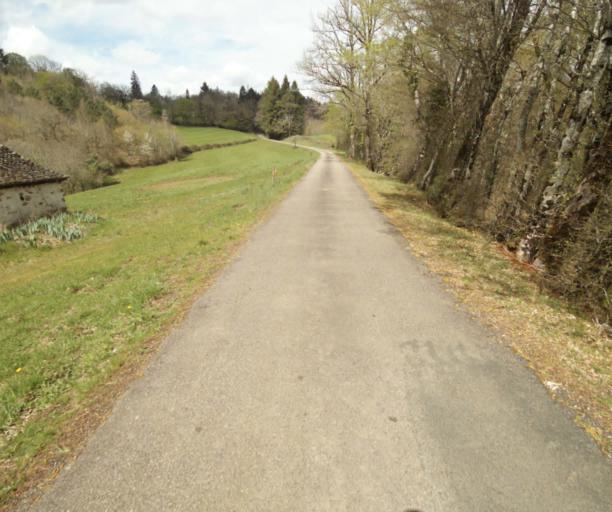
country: FR
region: Limousin
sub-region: Departement de la Correze
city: Sainte-Fortunade
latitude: 45.1881
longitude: 1.8662
